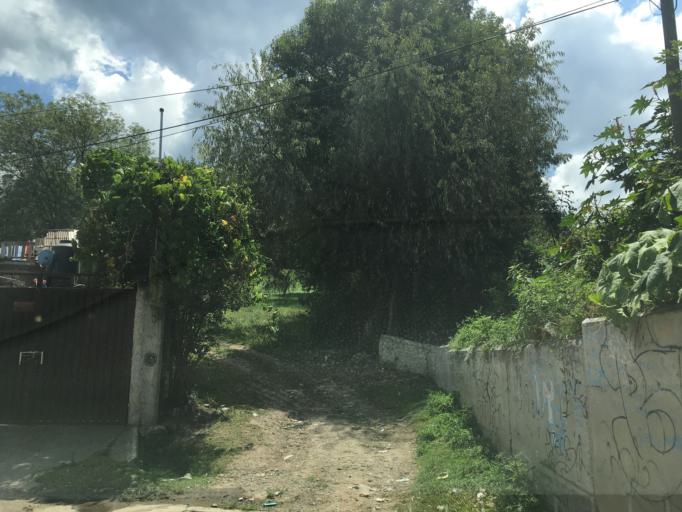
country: MX
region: Michoacan
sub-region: Morelia
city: Morelos
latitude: 19.6475
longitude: -101.2413
